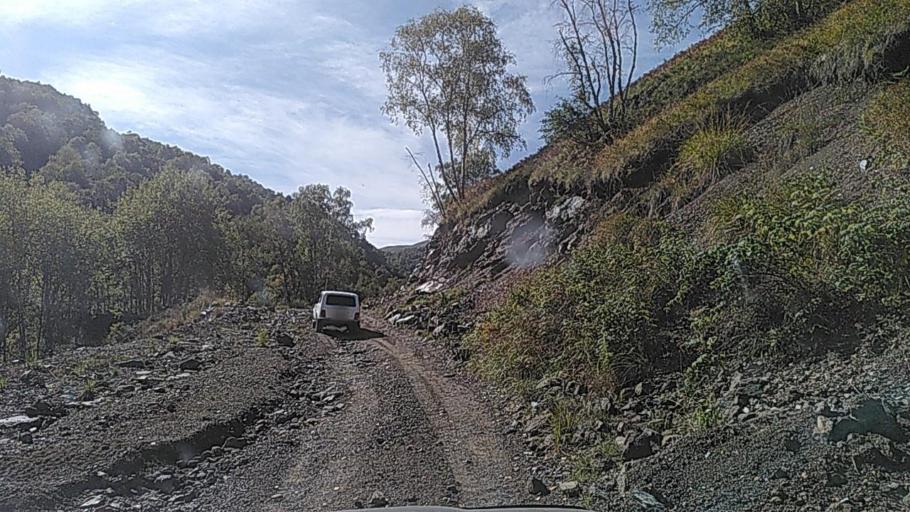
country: RU
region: Kabardino-Balkariya
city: Kamennomostskoye
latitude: 43.7054
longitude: 42.8453
